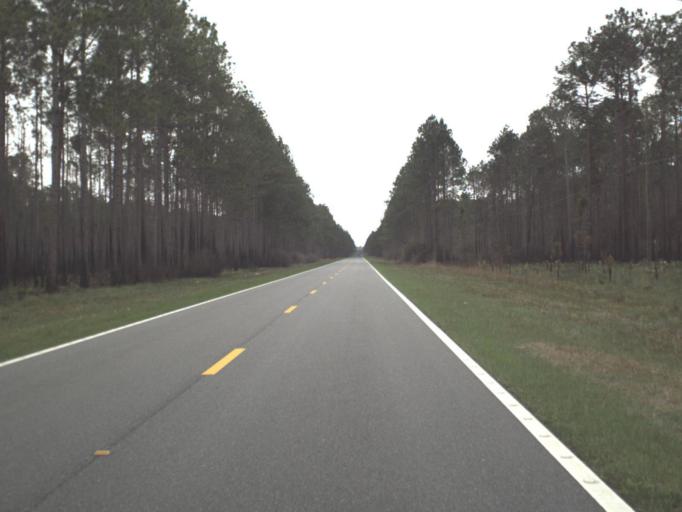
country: US
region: Florida
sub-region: Gulf County
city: Wewahitchka
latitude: 30.0539
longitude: -84.9835
